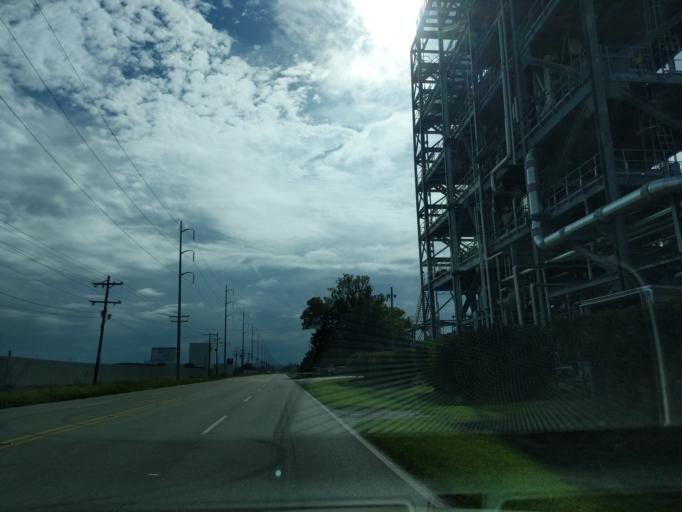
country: US
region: Louisiana
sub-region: Saint Bernard Parish
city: Chalmette
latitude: 30.0350
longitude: -89.9084
